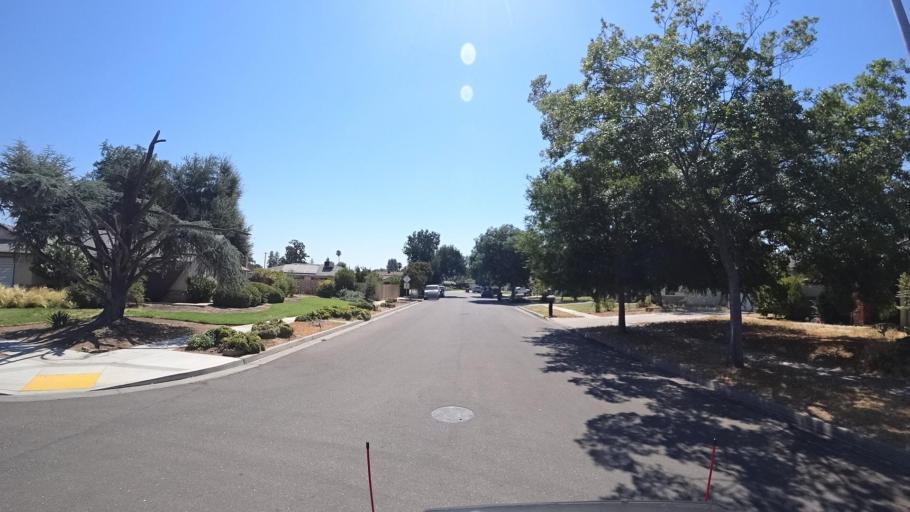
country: US
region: California
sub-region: Fresno County
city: Sunnyside
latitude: 36.7482
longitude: -119.6966
